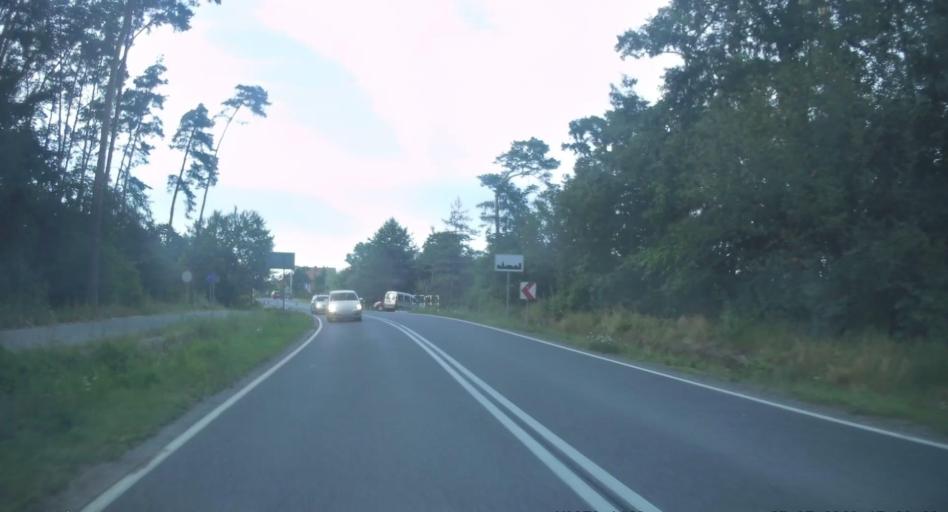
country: PL
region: Lesser Poland Voivodeship
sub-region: Powiat brzeski
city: Przyborow
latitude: 50.0574
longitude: 20.6396
